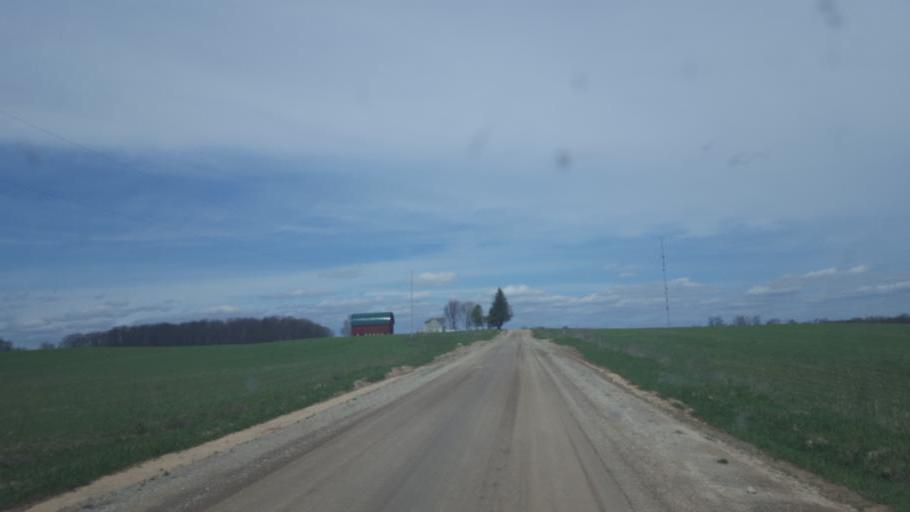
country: US
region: Michigan
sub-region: Isabella County
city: Lake Isabella
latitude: 43.6132
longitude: -84.8881
